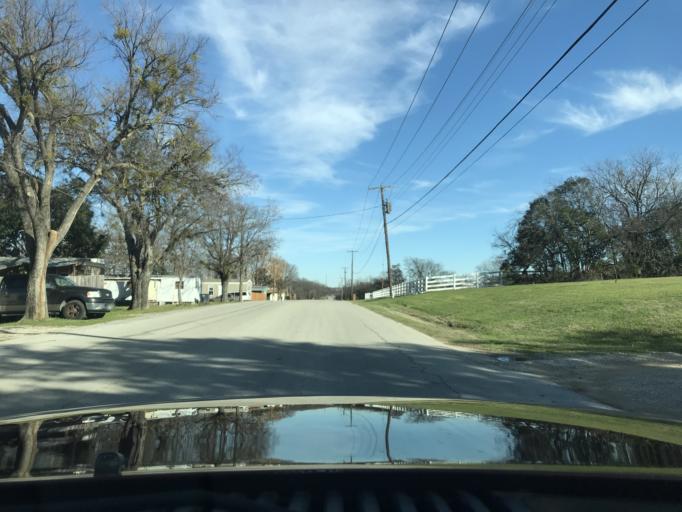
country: US
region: Texas
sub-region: Tarrant County
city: Edgecliff Village
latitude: 32.6614
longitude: -97.3468
